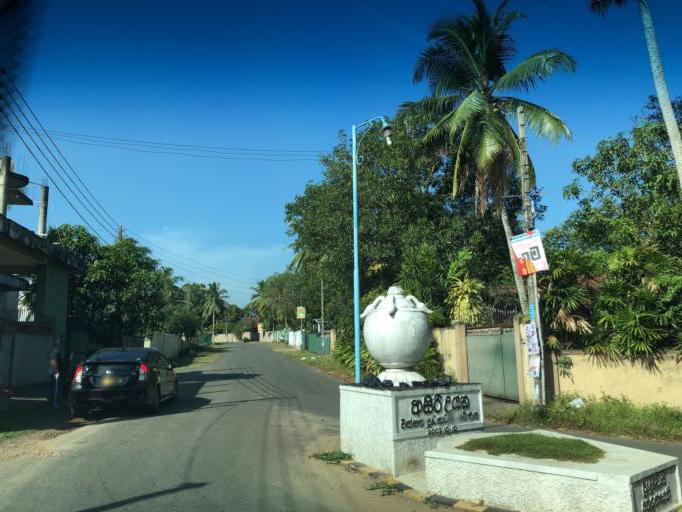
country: LK
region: Western
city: Homagama
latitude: 6.8091
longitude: 79.9772
